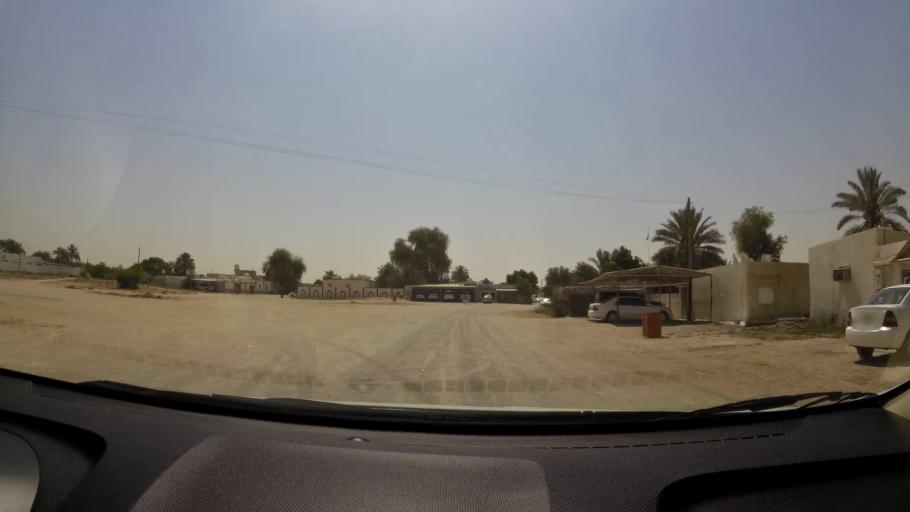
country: AE
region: Ajman
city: Ajman
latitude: 25.3959
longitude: 55.5293
